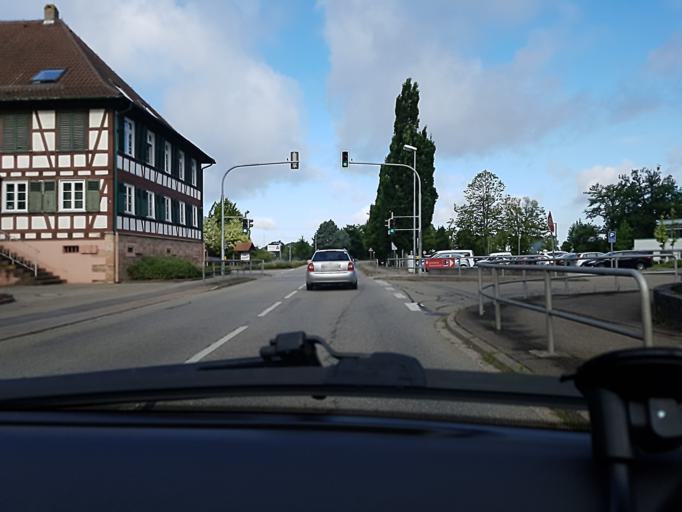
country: DE
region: Baden-Wuerttemberg
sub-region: Freiburg Region
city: Willstatt
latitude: 48.5649
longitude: 7.8670
